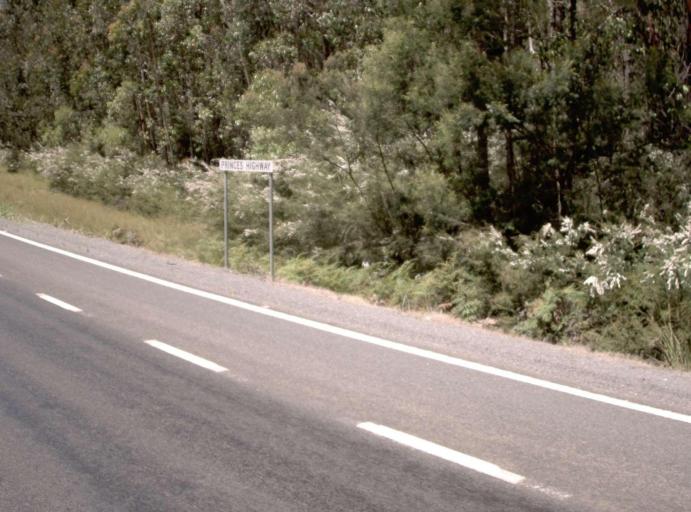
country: AU
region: Victoria
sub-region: East Gippsland
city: Lakes Entrance
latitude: -37.6901
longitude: 148.6174
